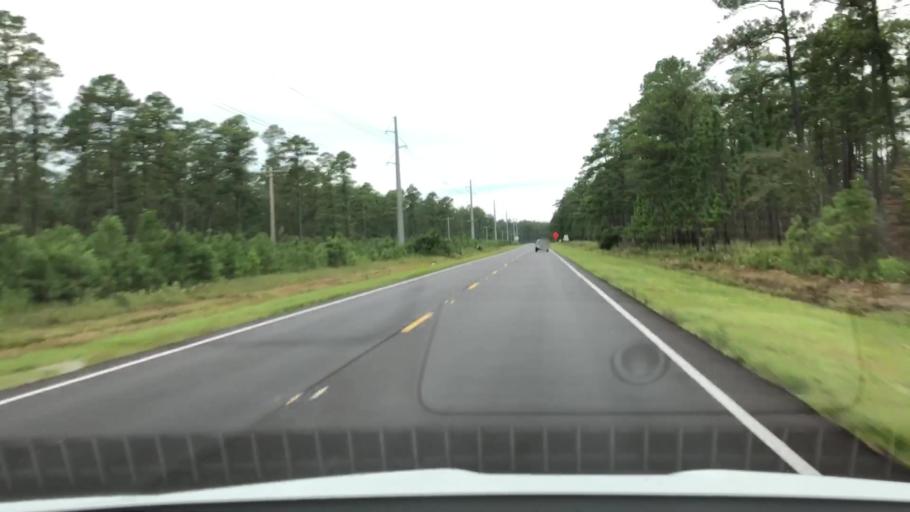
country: US
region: North Carolina
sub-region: Onslow County
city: Swansboro
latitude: 34.8120
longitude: -77.1386
